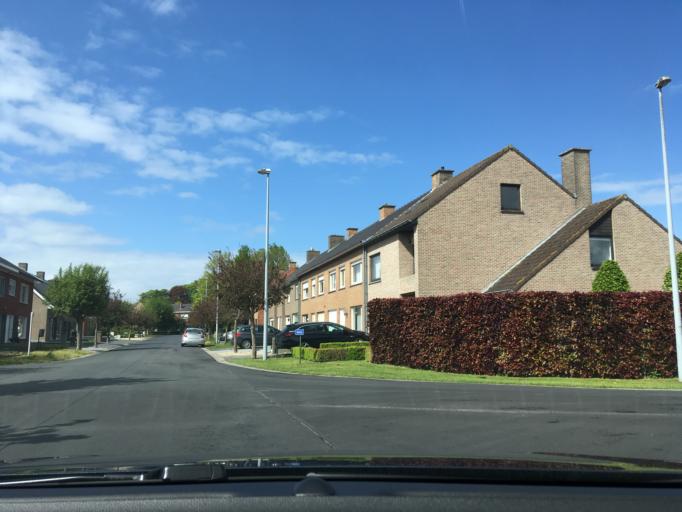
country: BE
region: Flanders
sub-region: Provincie West-Vlaanderen
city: Tielt
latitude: 51.0013
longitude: 3.3355
